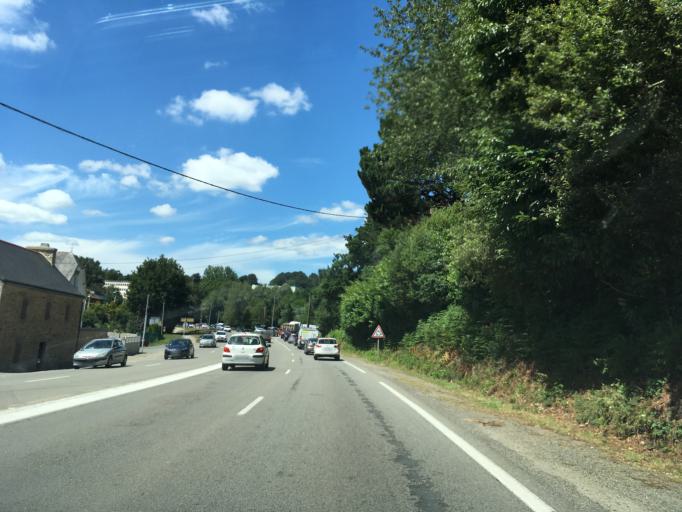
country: FR
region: Brittany
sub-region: Departement du Finistere
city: Quimper
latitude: 47.9777
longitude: -4.0935
